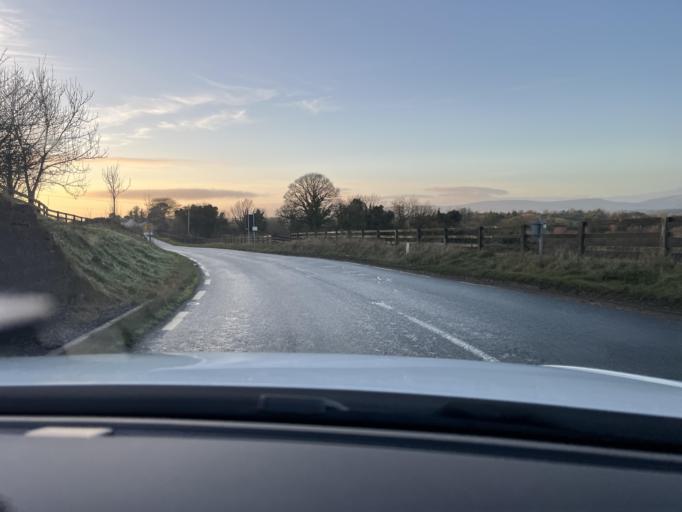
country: IE
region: Ulster
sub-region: An Cabhan
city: Ballyconnell
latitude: 54.0813
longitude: -7.6647
